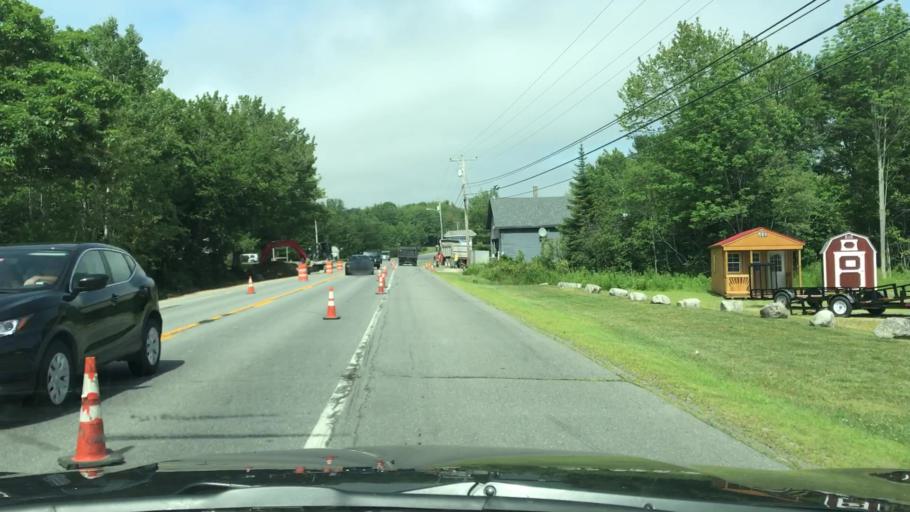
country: US
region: Maine
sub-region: Waldo County
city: Stockton Springs
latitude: 44.4789
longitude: -68.8756
